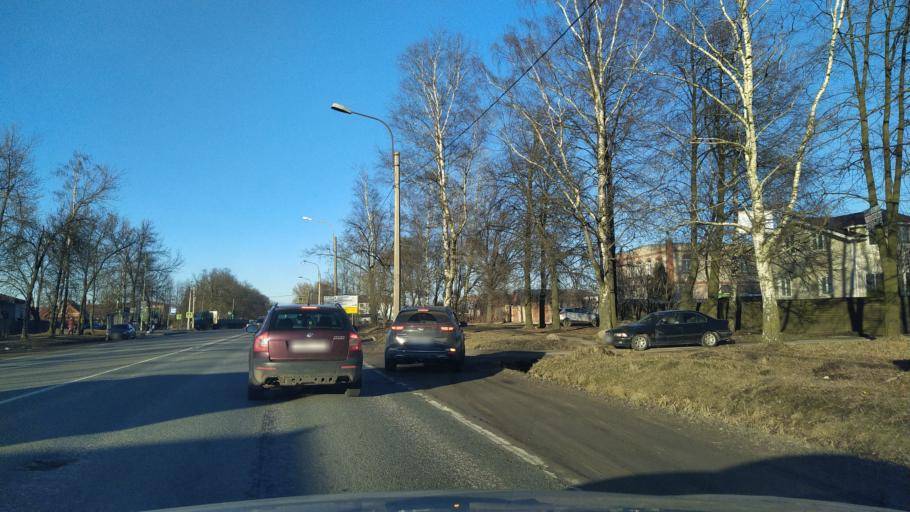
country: RU
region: St.-Petersburg
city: Gorelovo
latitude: 59.7798
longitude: 30.1328
